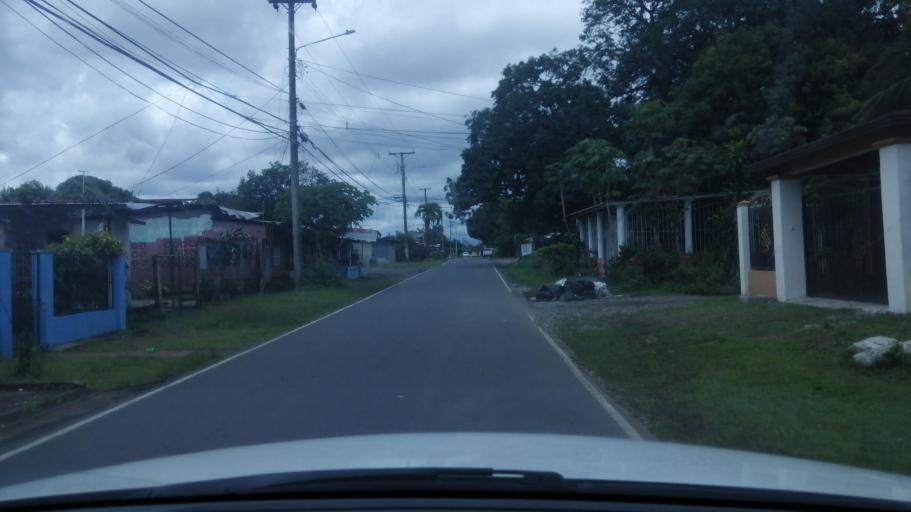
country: PA
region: Chiriqui
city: David
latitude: 8.4216
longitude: -82.4274
